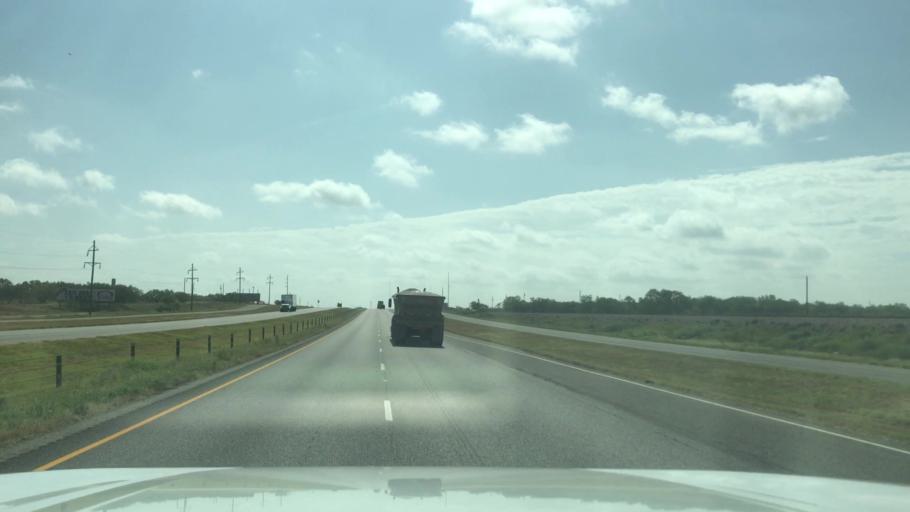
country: US
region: Texas
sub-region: Taylor County
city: Merkel
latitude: 32.4756
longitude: -100.0473
